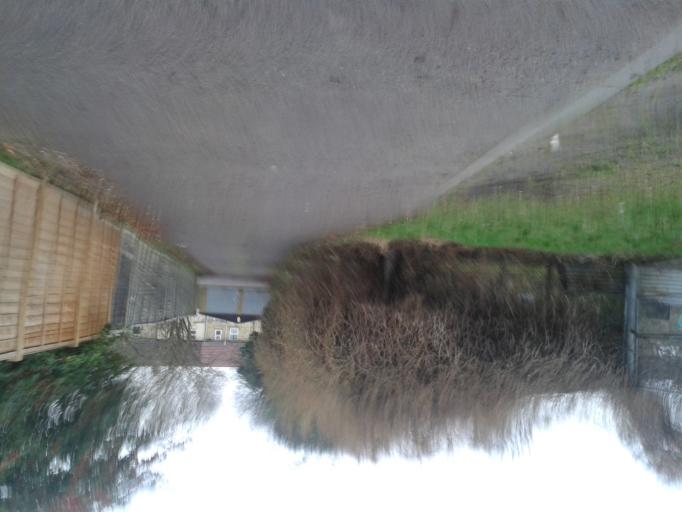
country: GB
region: England
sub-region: Cambridgeshire
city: Cambridge
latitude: 52.2037
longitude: 0.1541
